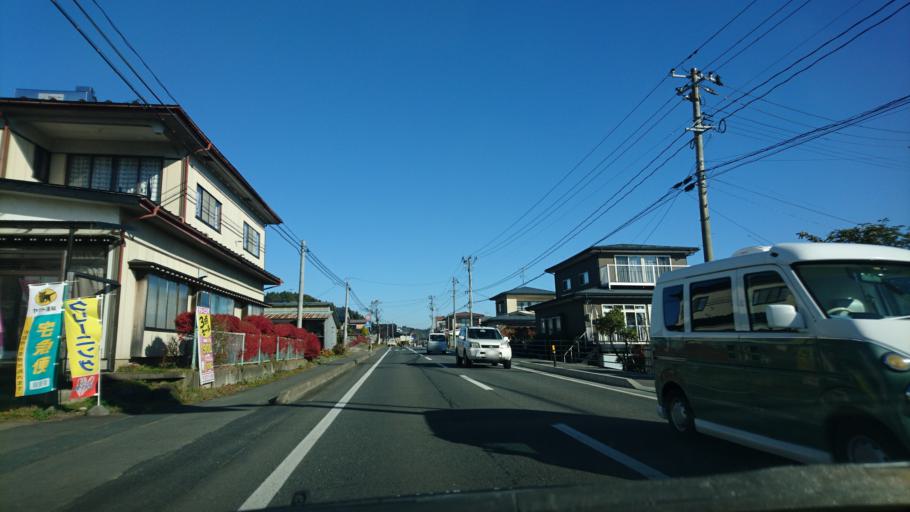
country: JP
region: Iwate
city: Mizusawa
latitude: 39.0597
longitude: 141.1244
